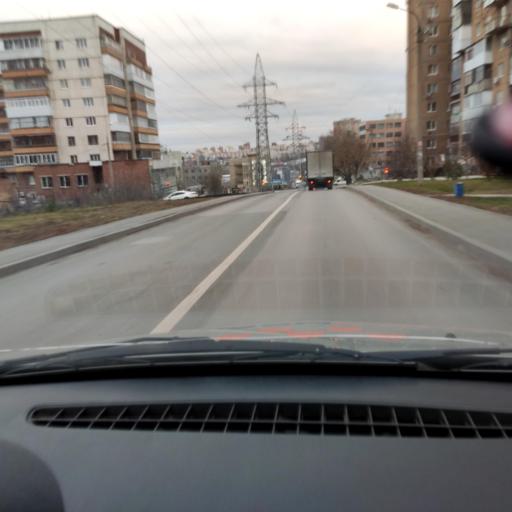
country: RU
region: Bashkortostan
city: Ufa
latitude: 54.7103
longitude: 55.9904
